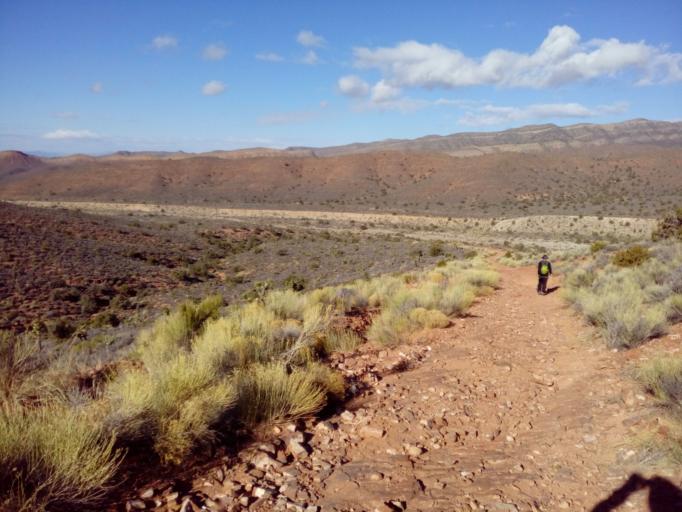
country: US
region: Nevada
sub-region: Clark County
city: Summerlin South
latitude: 36.0789
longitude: -115.5720
